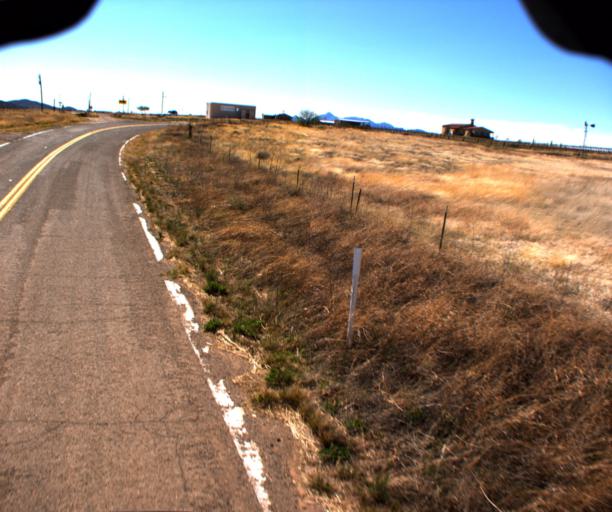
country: US
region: Arizona
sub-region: Cochise County
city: Huachuca City
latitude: 31.6080
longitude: -110.5855
